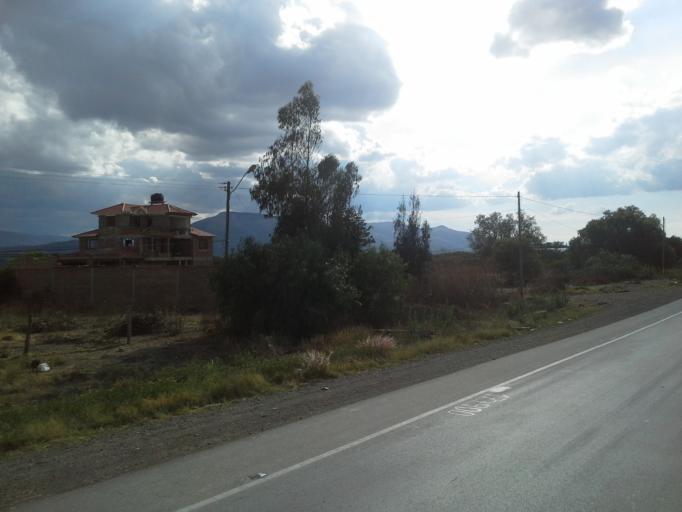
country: BO
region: Cochabamba
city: Tarata
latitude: -17.5444
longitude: -66.0165
